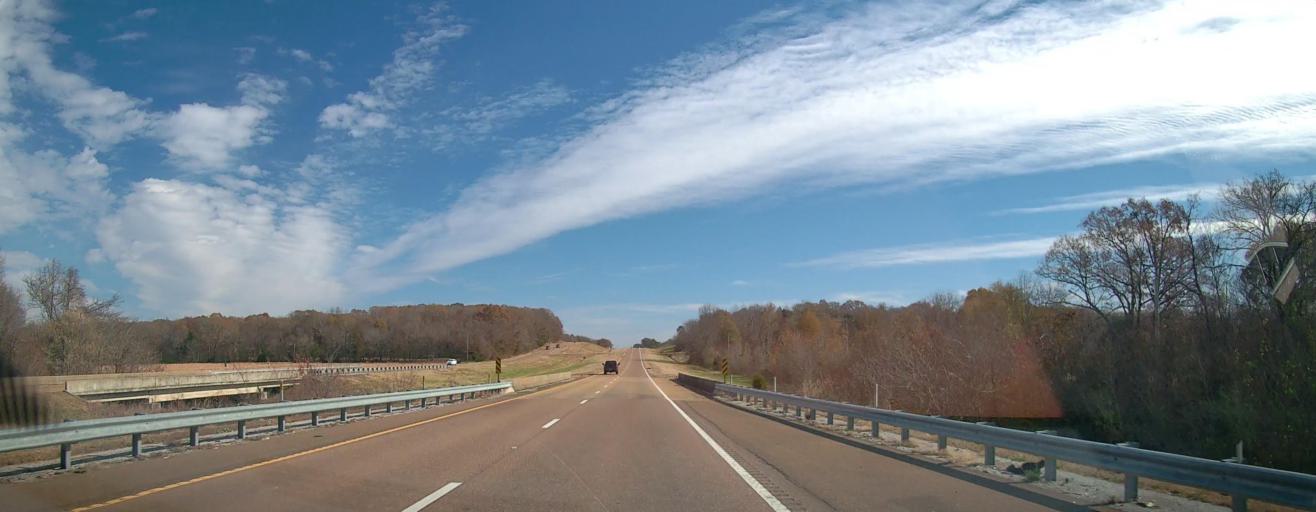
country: US
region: Mississippi
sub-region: Benton County
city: Ashland
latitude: 34.9460
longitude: -89.3445
